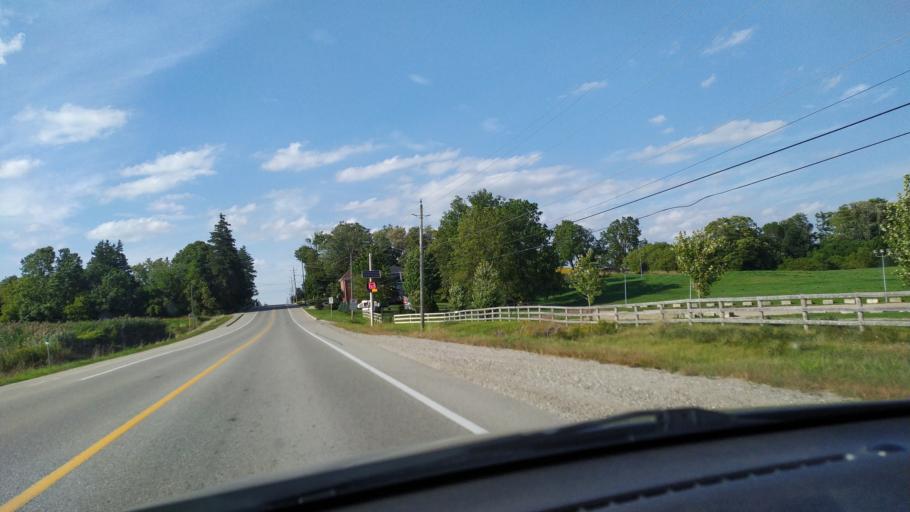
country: CA
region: Ontario
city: Ingersoll
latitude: 43.1512
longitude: -80.8988
